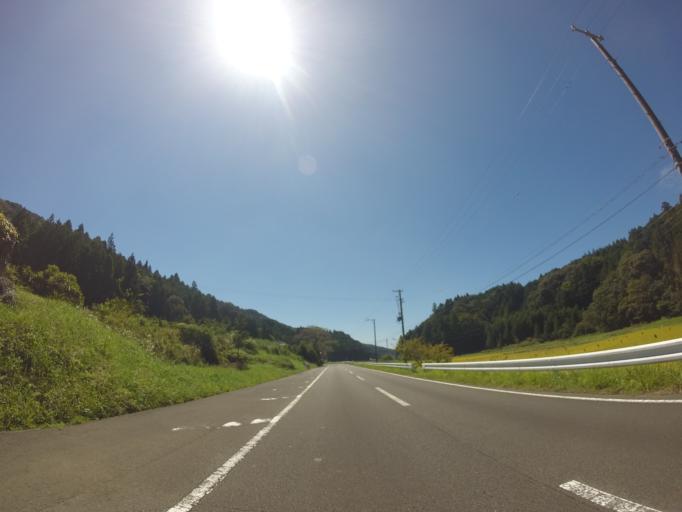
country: JP
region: Shizuoka
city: Kanaya
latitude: 34.8886
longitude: 138.1484
